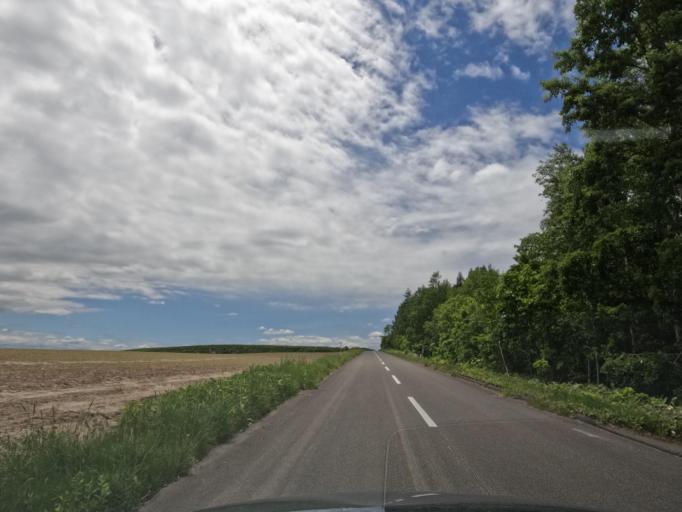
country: JP
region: Hokkaido
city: Shimo-furano
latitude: 43.5096
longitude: 142.4209
